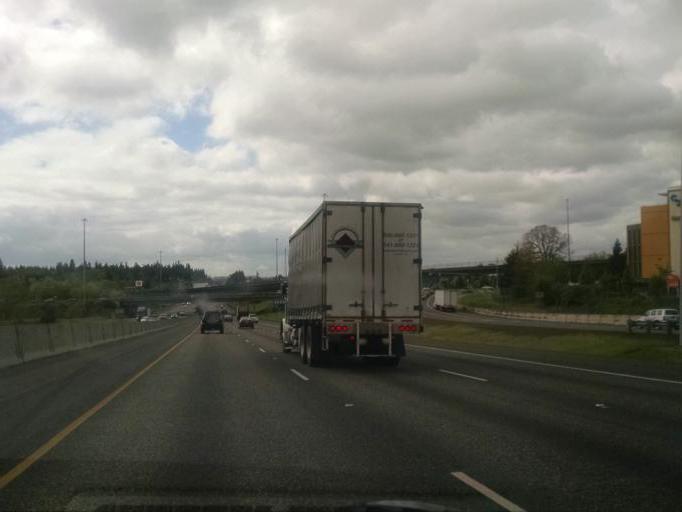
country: US
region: Oregon
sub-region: Washington County
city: Durham
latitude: 45.4235
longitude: -122.7442
